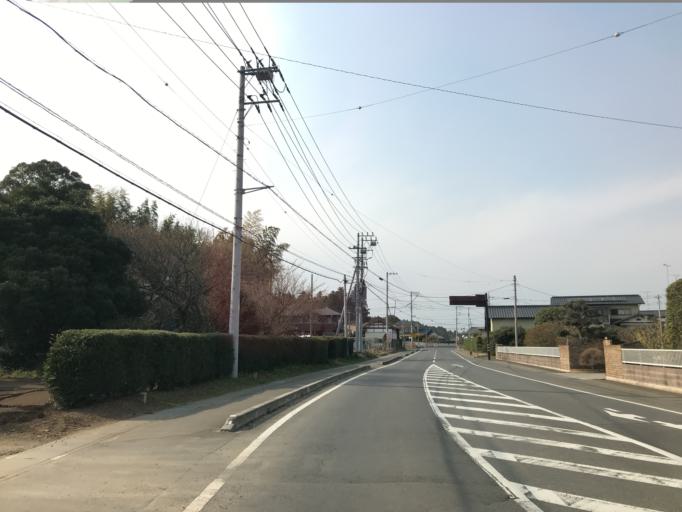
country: JP
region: Ibaraki
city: Okunoya
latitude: 36.2180
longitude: 140.4094
